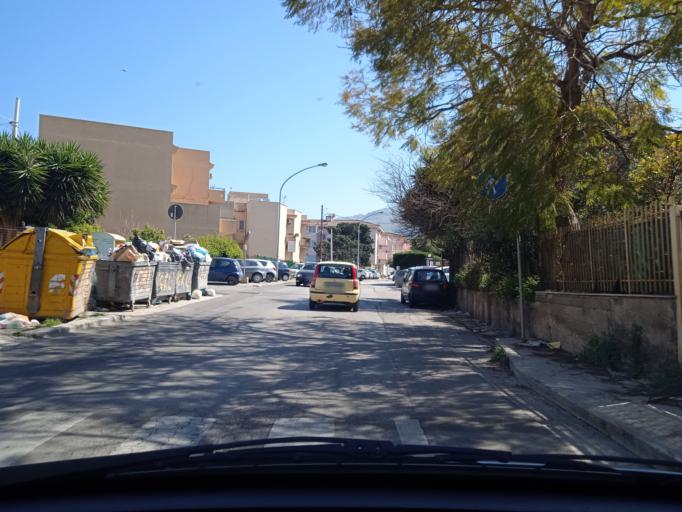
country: IT
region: Sicily
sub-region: Palermo
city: Villabate
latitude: 38.0908
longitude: 13.4322
